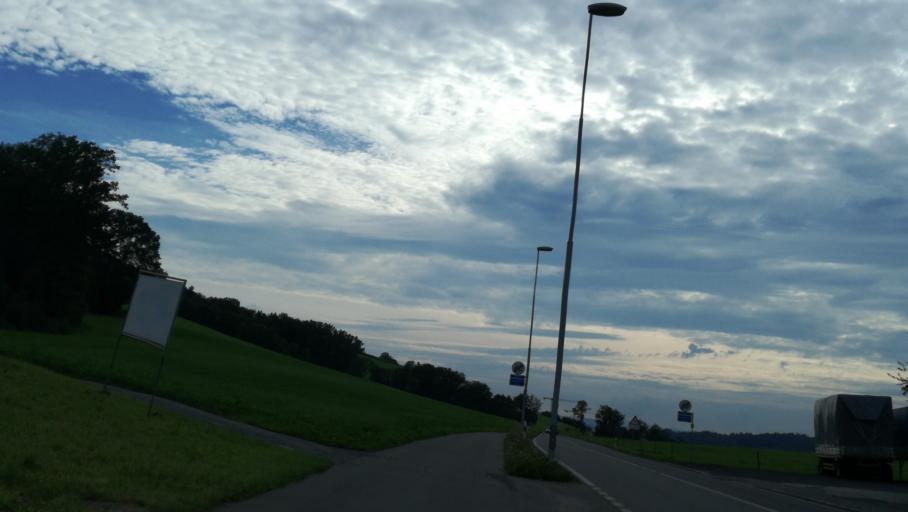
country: CH
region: Lucerne
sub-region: Lucerne-Land District
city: Meierskappel
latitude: 47.1381
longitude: 8.4226
